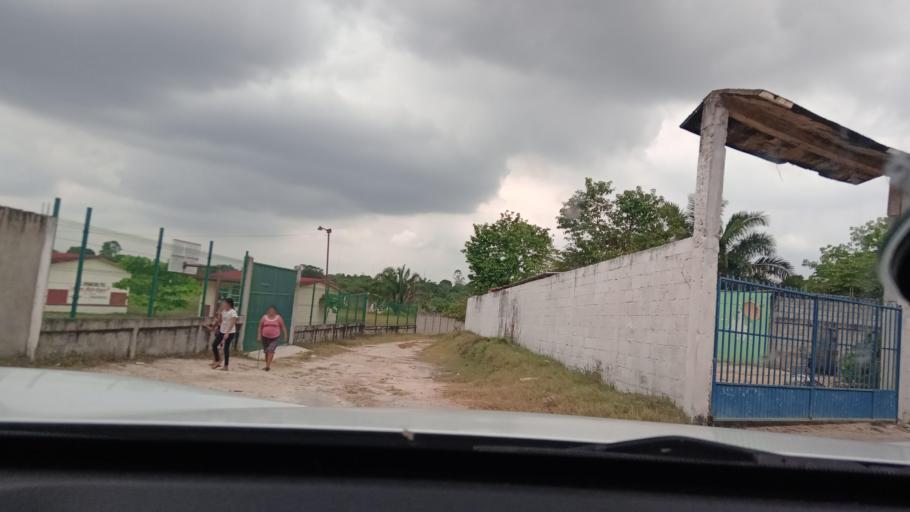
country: MX
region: Veracruz
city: Las Choapas
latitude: 17.8907
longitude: -94.1090
